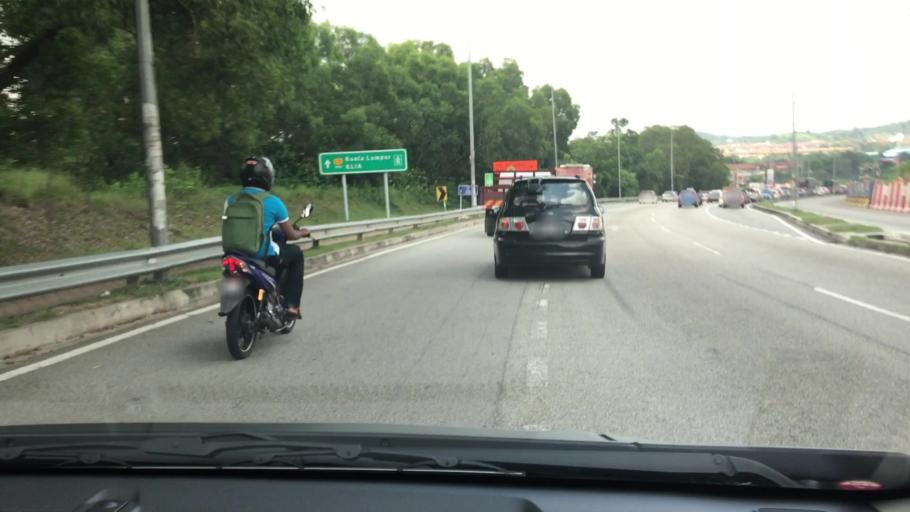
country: MY
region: Putrajaya
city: Putrajaya
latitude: 2.9845
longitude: 101.6621
